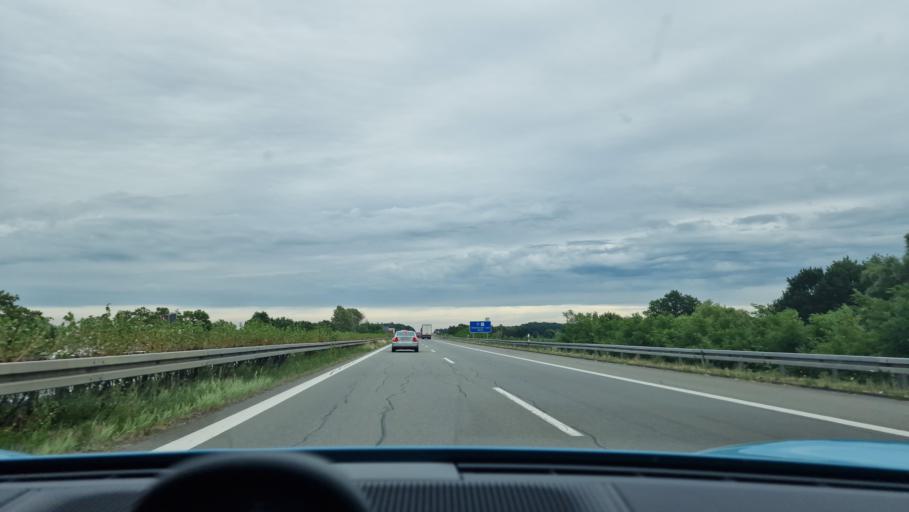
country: DE
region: Mecklenburg-Vorpommern
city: Wittenburg
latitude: 53.4968
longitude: 11.1040
